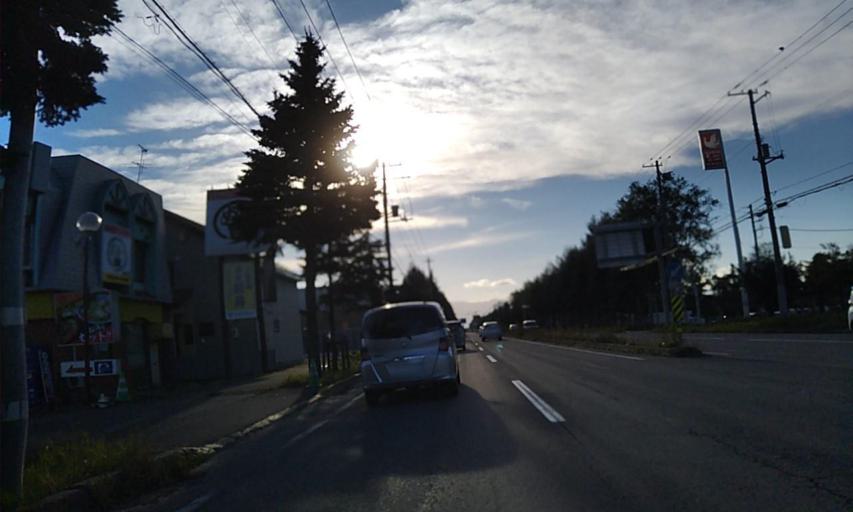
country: JP
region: Hokkaido
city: Obihiro
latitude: 42.9266
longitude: 143.1289
